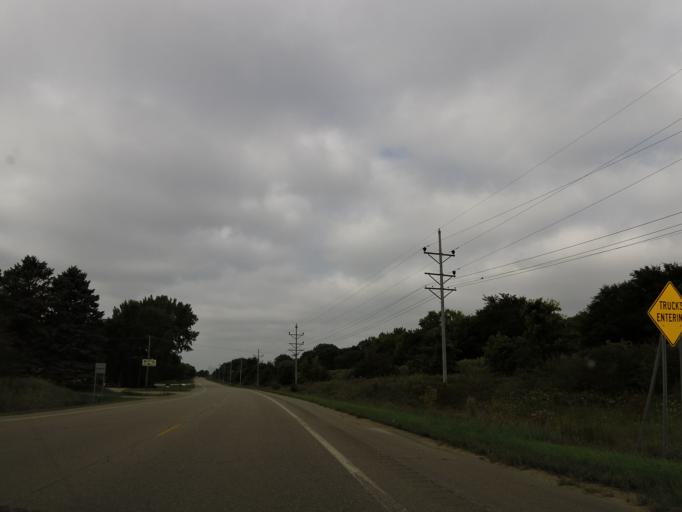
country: US
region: Minnesota
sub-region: Chippewa County
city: Montevideo
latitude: 44.9183
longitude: -95.6966
